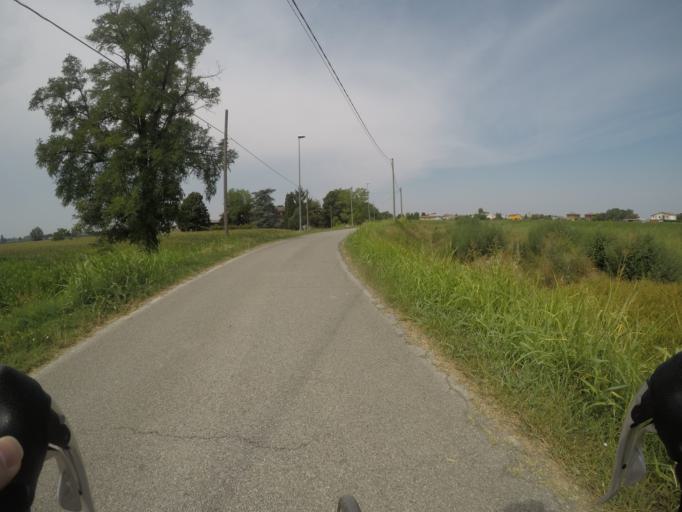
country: IT
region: Veneto
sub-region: Provincia di Rovigo
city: Villanova del Ghebbo Canton
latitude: 45.0496
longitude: 11.6569
